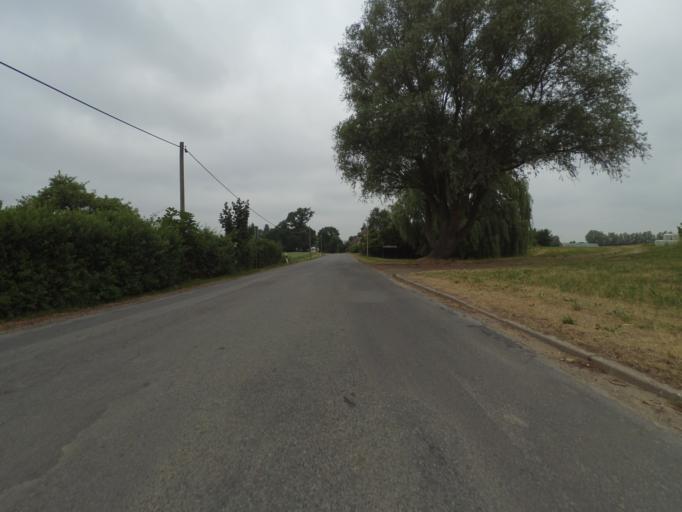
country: DE
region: Mecklenburg-Vorpommern
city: Lubz
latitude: 53.5003
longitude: 11.9605
